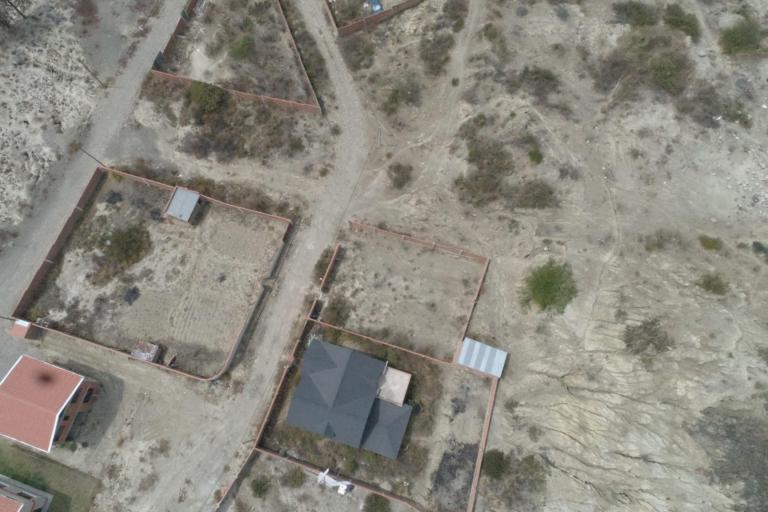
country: BO
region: La Paz
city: La Paz
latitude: -16.5976
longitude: -68.0701
